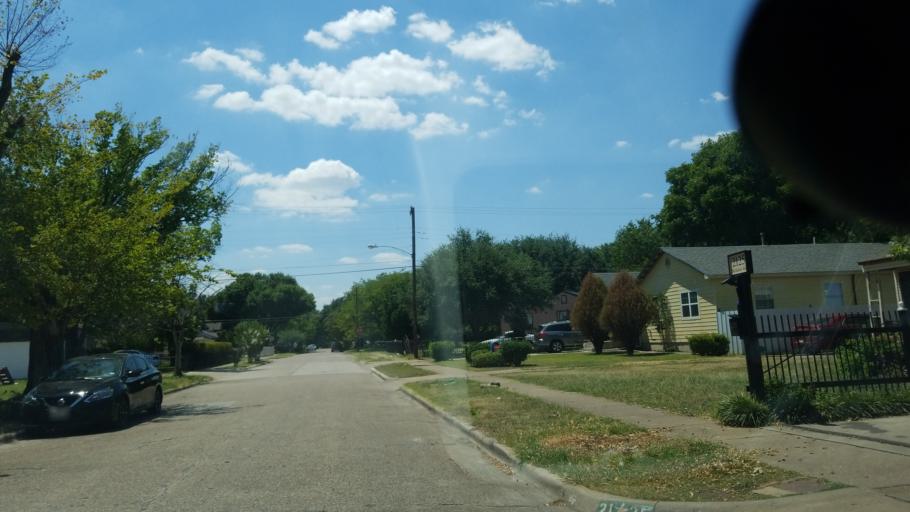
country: US
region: Texas
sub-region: Dallas County
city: Cockrell Hill
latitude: 32.7152
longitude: -96.8534
